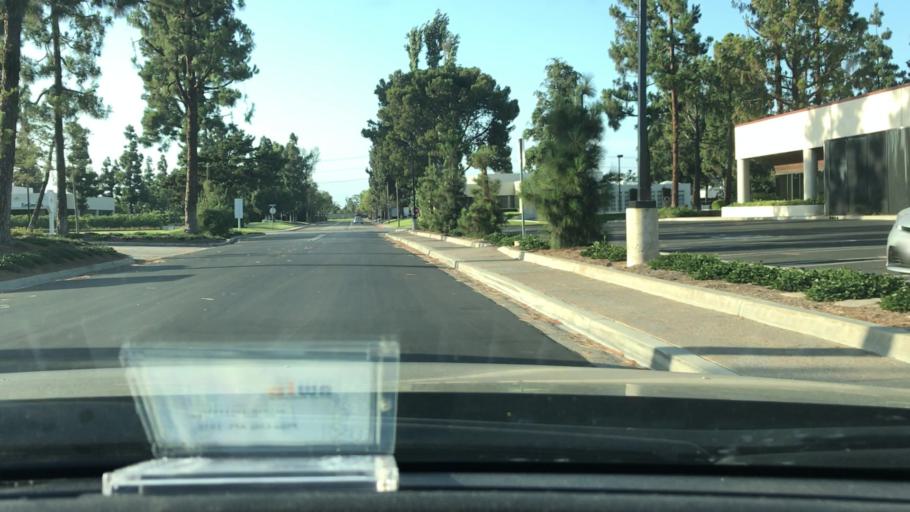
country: US
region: California
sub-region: Orange County
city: Fountain Valley
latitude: 33.6984
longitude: -117.9239
